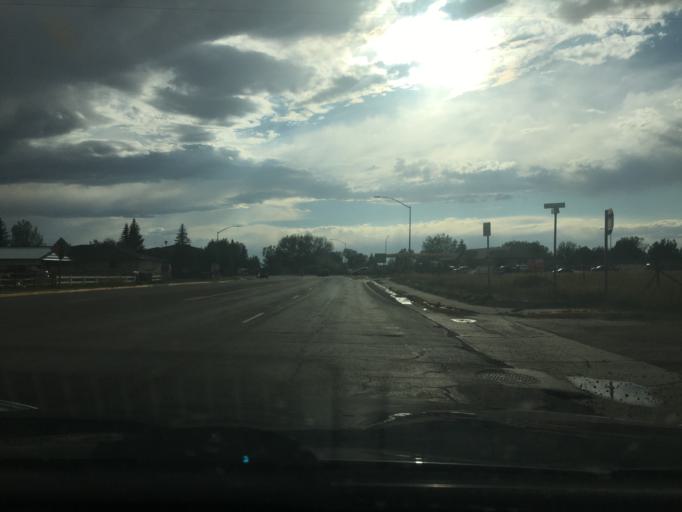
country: US
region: Wyoming
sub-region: Albany County
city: Laramie
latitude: 41.3090
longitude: -105.6276
